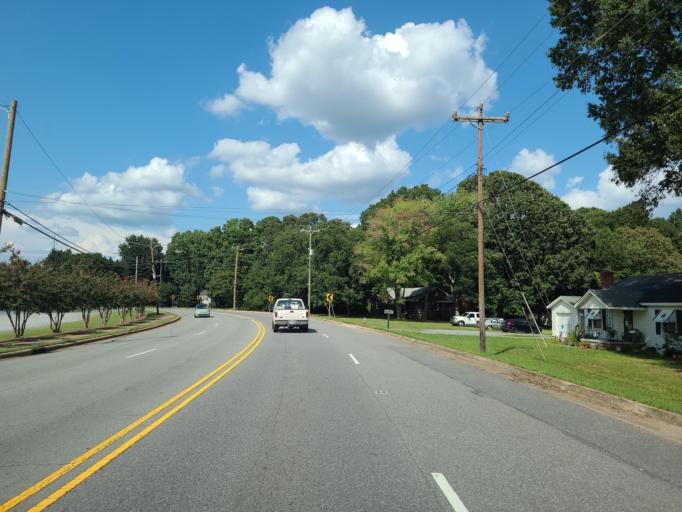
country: US
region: North Carolina
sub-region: Gaston County
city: Lowell
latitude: 35.2704
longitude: -81.0966
